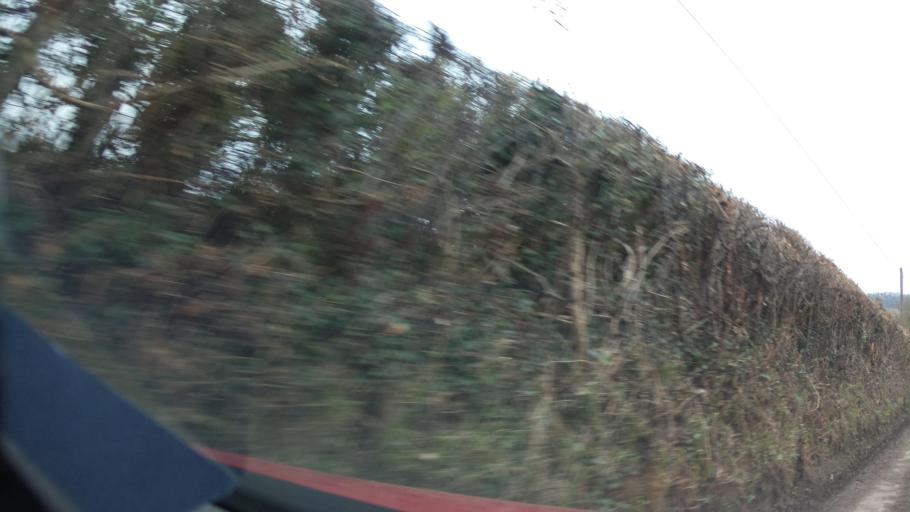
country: GB
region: England
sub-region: Wiltshire
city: Biddestone
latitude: 51.4664
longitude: -2.2336
